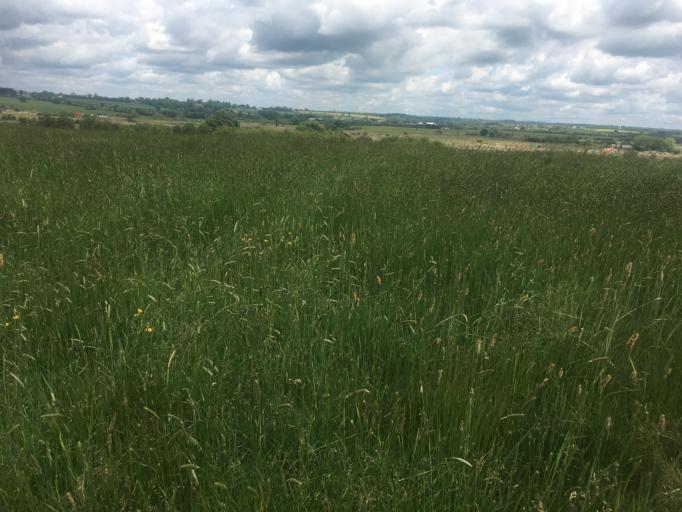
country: GB
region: England
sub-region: Warwickshire
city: Rugby
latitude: 52.3619
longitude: -1.1976
